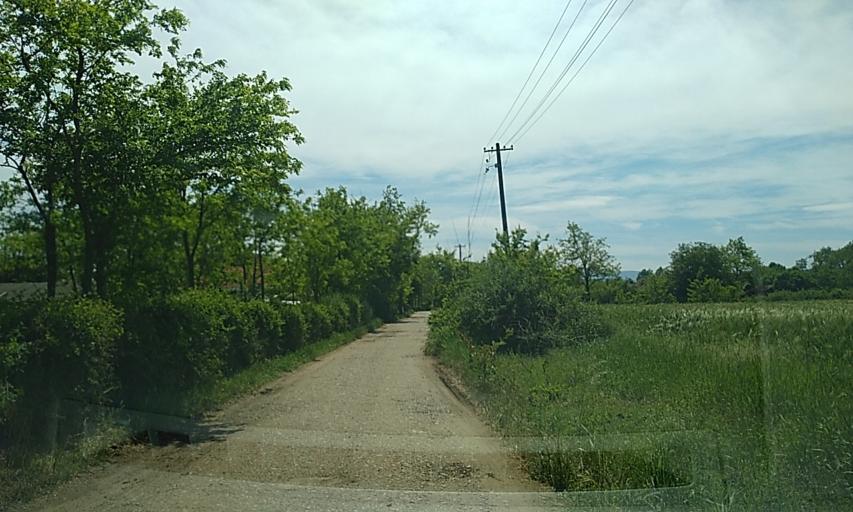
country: RS
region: Central Serbia
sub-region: Nisavski Okrug
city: Razanj
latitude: 43.5987
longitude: 21.6197
